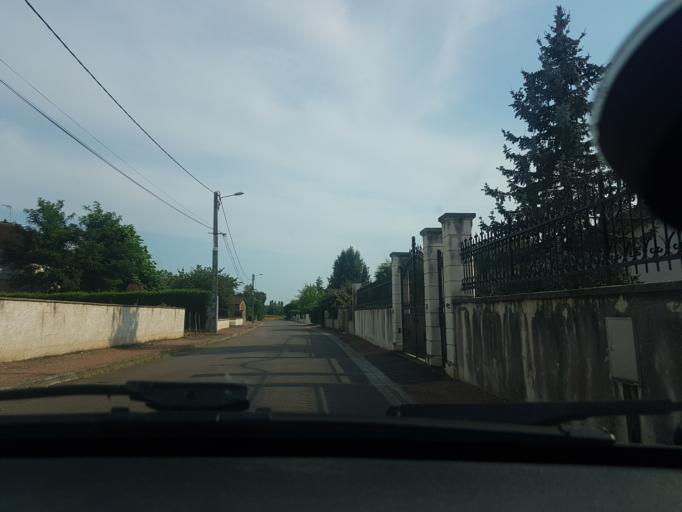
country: FR
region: Bourgogne
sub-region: Departement de Saone-et-Loire
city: Saint-Marcel
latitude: 46.7660
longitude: 4.8892
